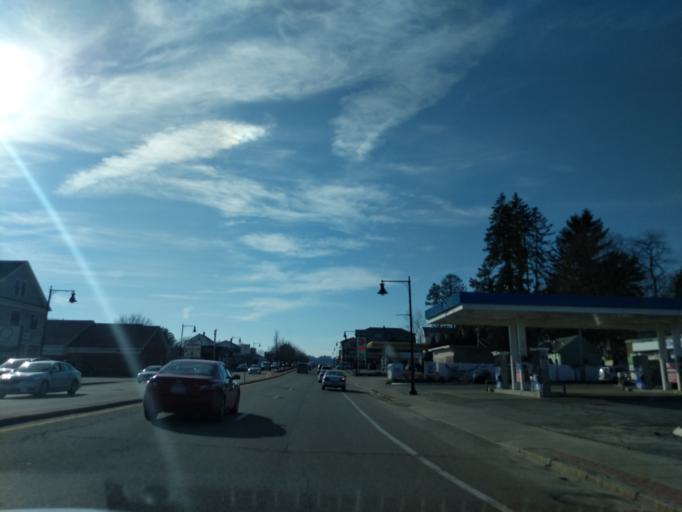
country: US
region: Massachusetts
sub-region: Worcester County
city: Shrewsbury
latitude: 42.2757
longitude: -71.7384
